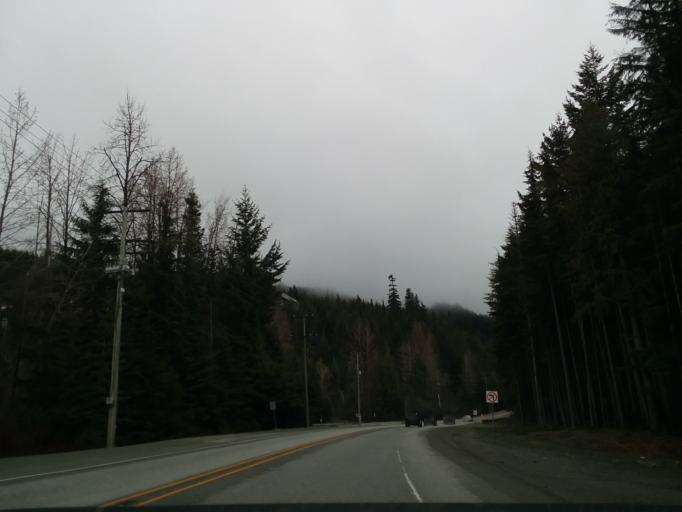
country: CA
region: British Columbia
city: Whistler
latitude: 50.1128
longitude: -122.9597
